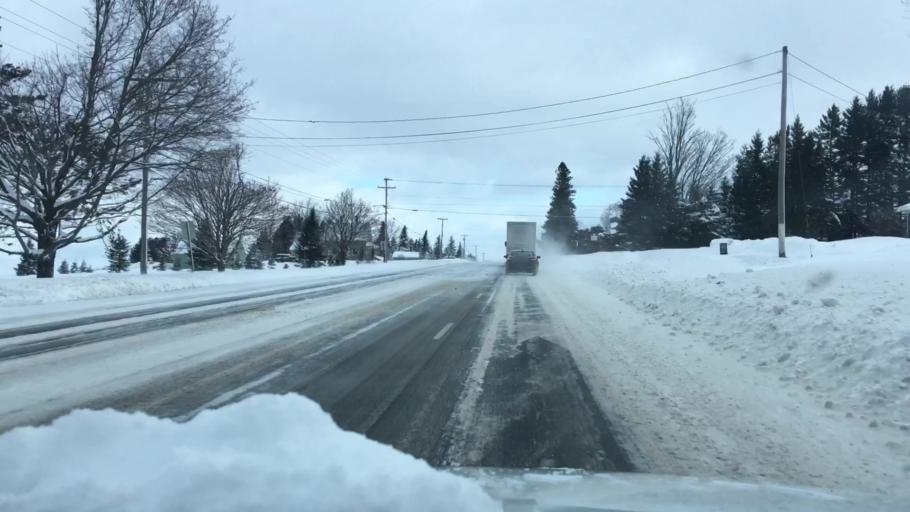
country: US
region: Maine
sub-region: Aroostook County
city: Presque Isle
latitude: 46.7269
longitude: -68.0036
